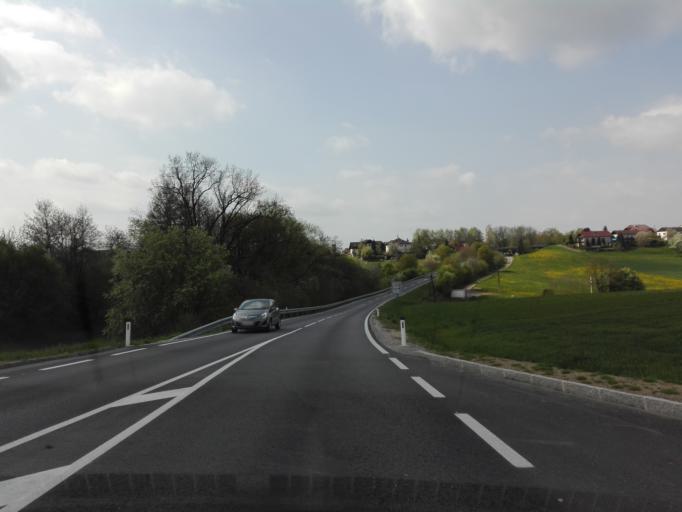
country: AT
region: Upper Austria
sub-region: Politischer Bezirk Perg
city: Perg
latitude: 48.2708
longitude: 14.7120
